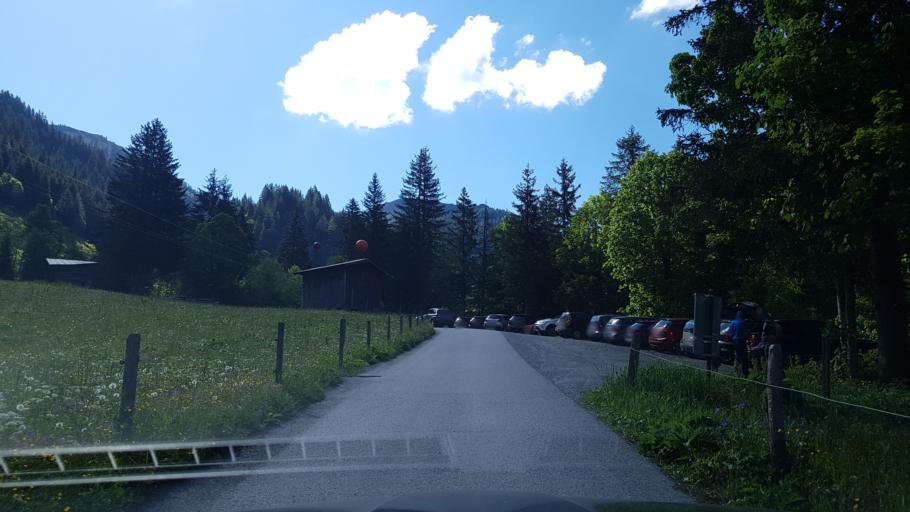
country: AT
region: Salzburg
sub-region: Politischer Bezirk Sankt Johann im Pongau
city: Kleinarl
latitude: 47.2359
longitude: 13.2655
